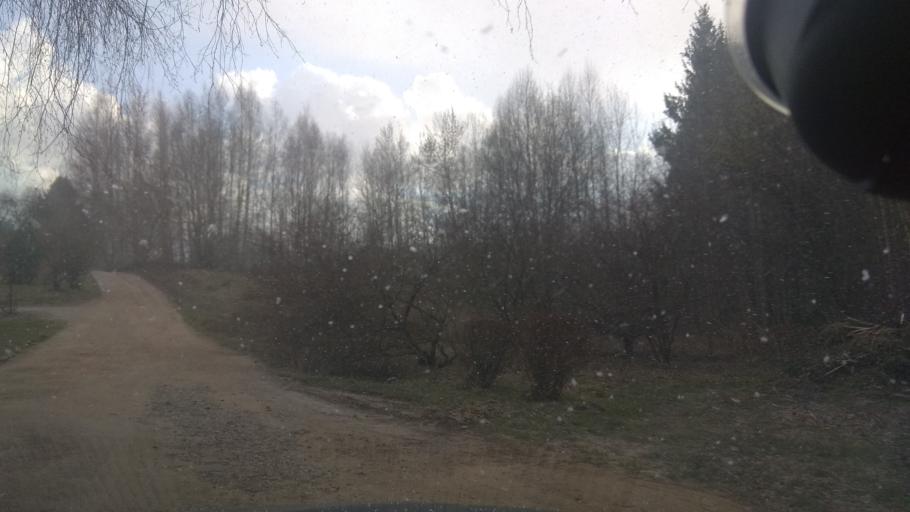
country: LT
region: Vilnius County
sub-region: Vilnius
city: Fabijoniskes
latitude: 54.7480
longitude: 25.2520
